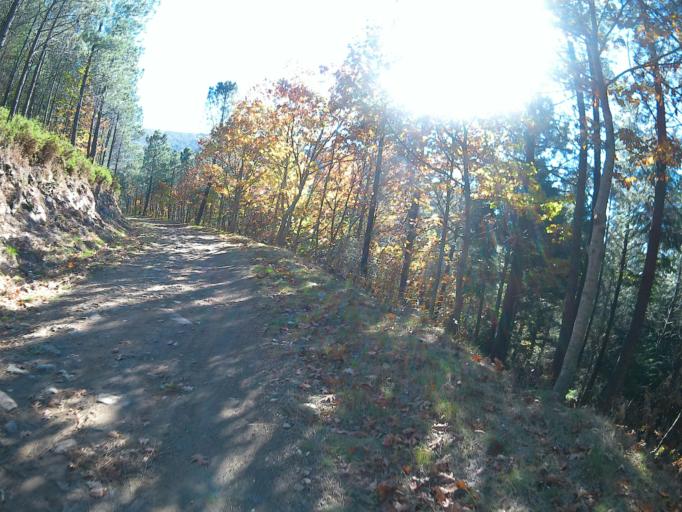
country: PT
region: Vila Real
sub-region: Mesao Frio
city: Mesao Frio
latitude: 41.2411
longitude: -7.9305
